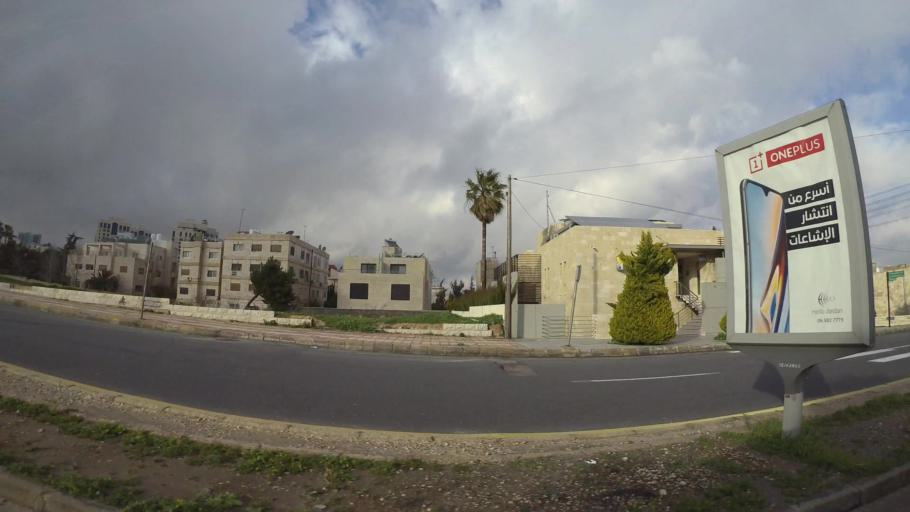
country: JO
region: Amman
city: Wadi as Sir
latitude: 31.9532
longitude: 35.8793
